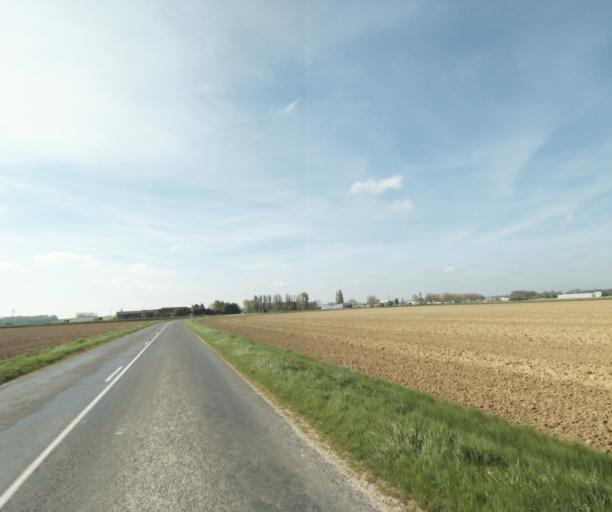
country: FR
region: Ile-de-France
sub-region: Departement de Seine-et-Marne
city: Nangis
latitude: 48.5663
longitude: 3.0391
